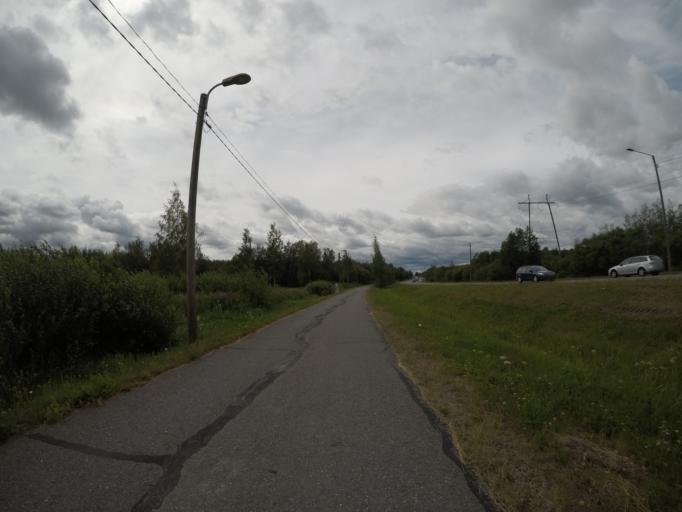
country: FI
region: Haeme
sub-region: Haemeenlinna
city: Haemeenlinna
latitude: 60.9772
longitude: 24.4966
